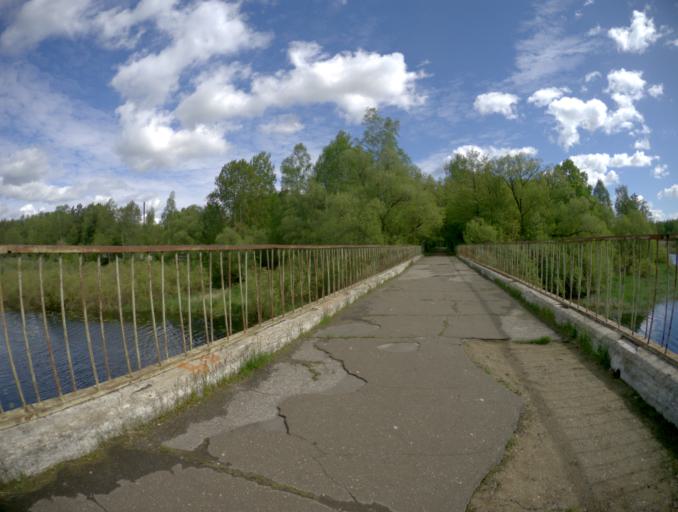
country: RU
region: Rjazan
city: Spas-Klepiki
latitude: 55.2417
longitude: 40.0462
